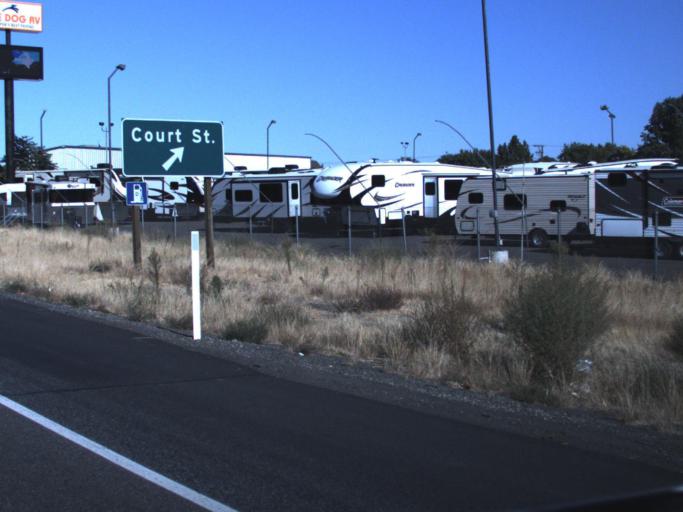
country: US
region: Washington
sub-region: Benton County
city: Kennewick
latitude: 46.2386
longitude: -119.1299
